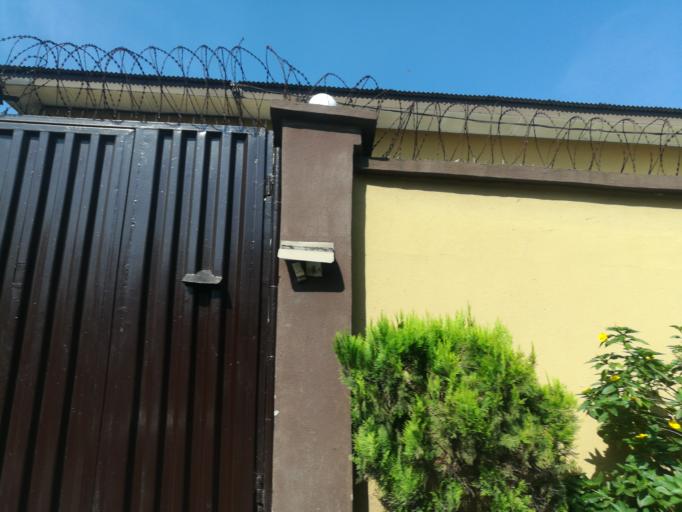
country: NG
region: Lagos
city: Ikeja
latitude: 6.6030
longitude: 3.3423
